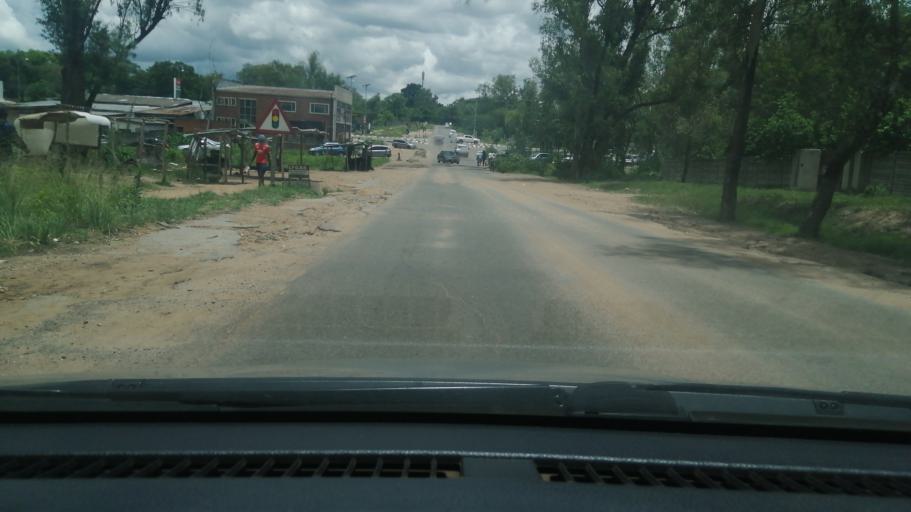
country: ZW
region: Harare
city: Harare
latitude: -17.8822
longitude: 31.0787
